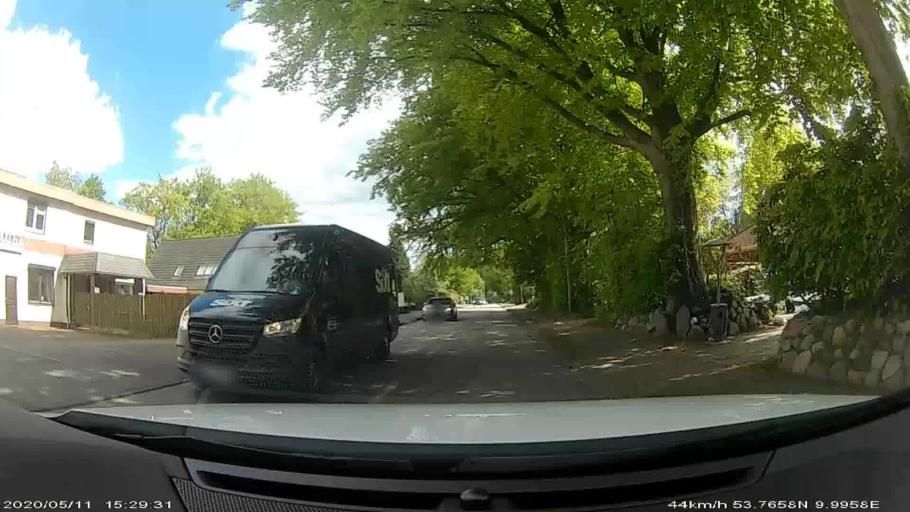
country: DE
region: Schleswig-Holstein
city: Henstedt-Ulzburg
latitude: 53.7568
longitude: 9.9967
